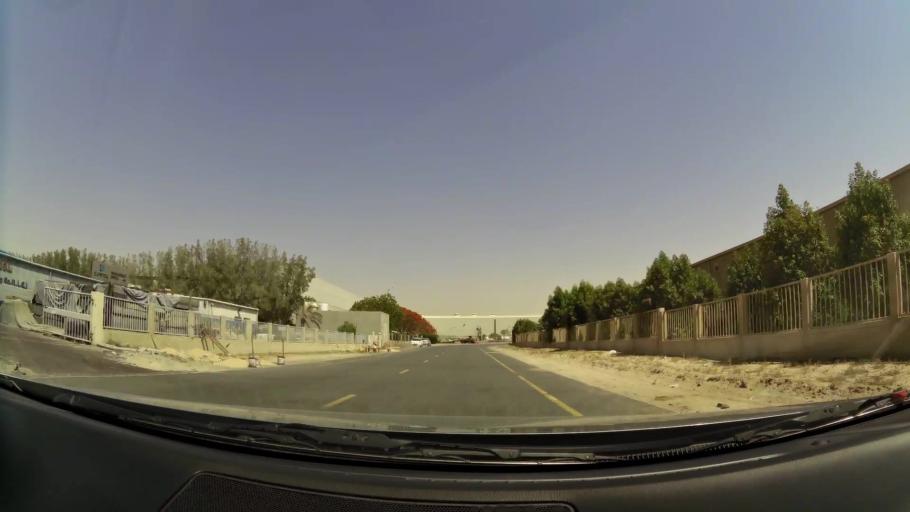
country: AE
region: Dubai
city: Dubai
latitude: 24.9875
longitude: 55.1596
